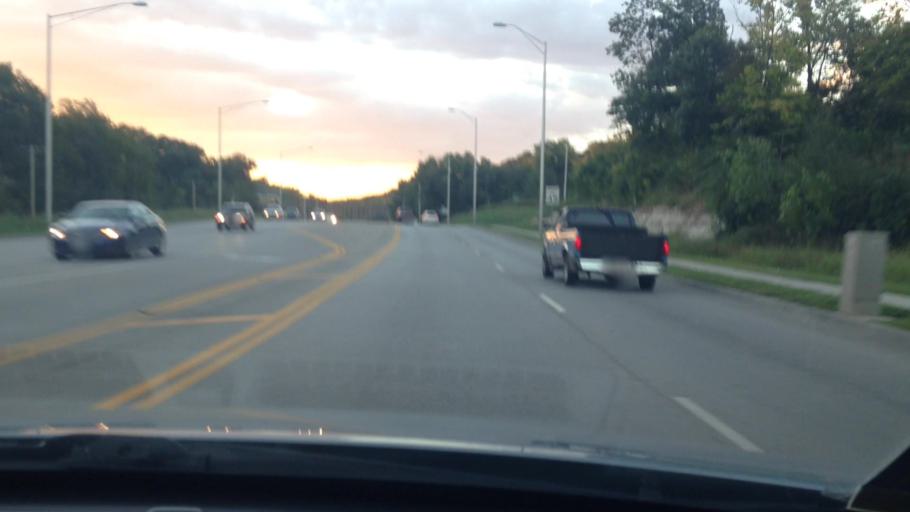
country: US
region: Missouri
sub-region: Jackson County
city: Raytown
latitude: 39.0300
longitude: -94.5094
